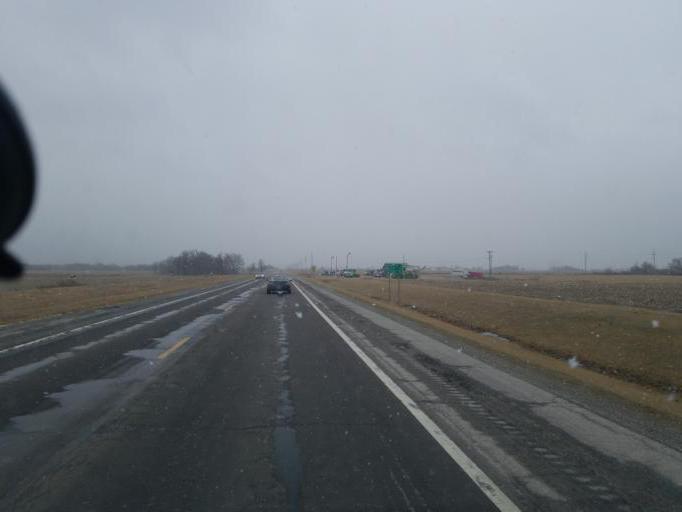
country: US
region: Missouri
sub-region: Schuyler County
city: Lancaster
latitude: 40.4018
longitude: -92.5591
